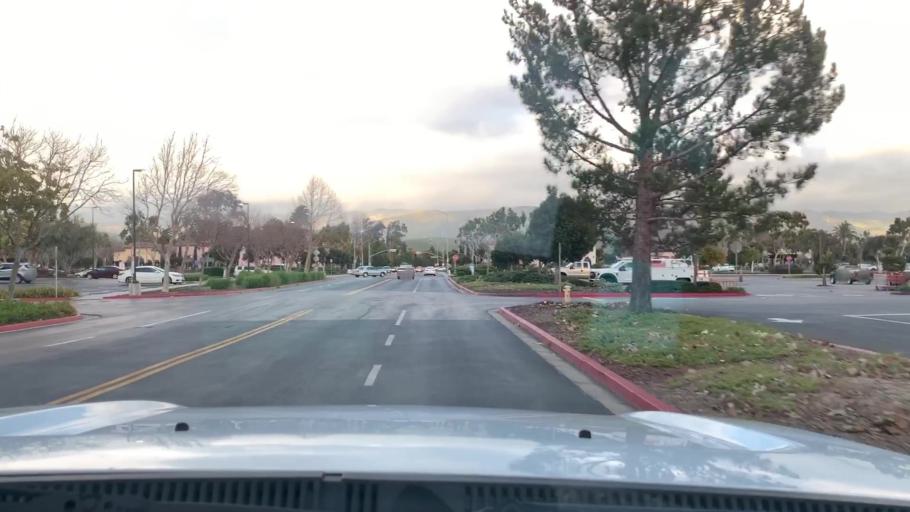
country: US
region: California
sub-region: San Luis Obispo County
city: San Luis Obispo
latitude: 35.2511
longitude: -120.6901
